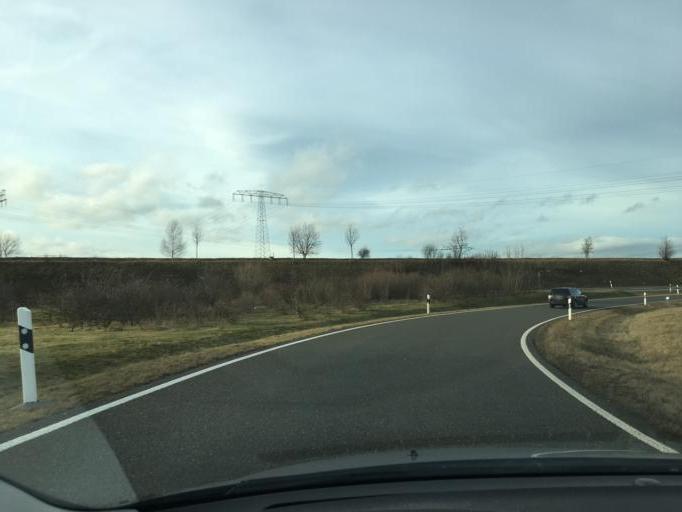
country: DE
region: Thuringia
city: Gerstenberg
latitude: 51.0218
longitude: 12.4565
